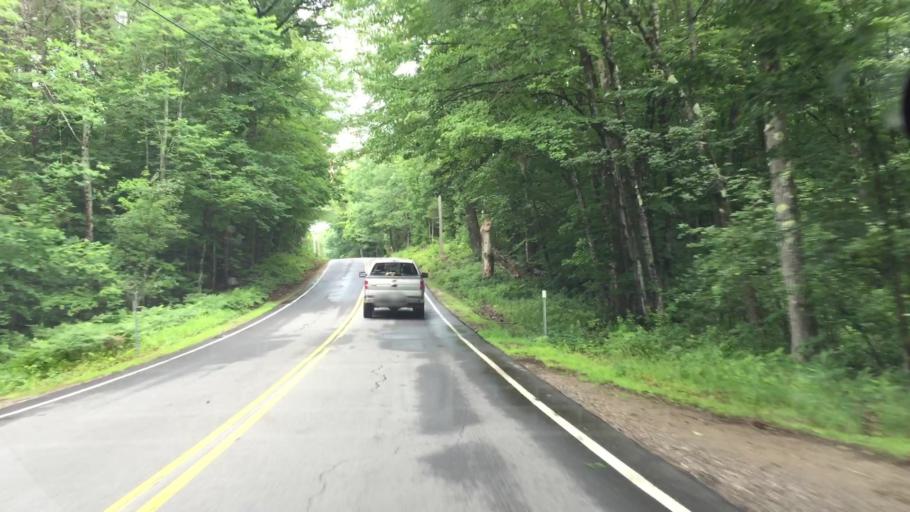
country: US
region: New Hampshire
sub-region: Carroll County
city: Sandwich
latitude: 43.8037
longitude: -71.4780
